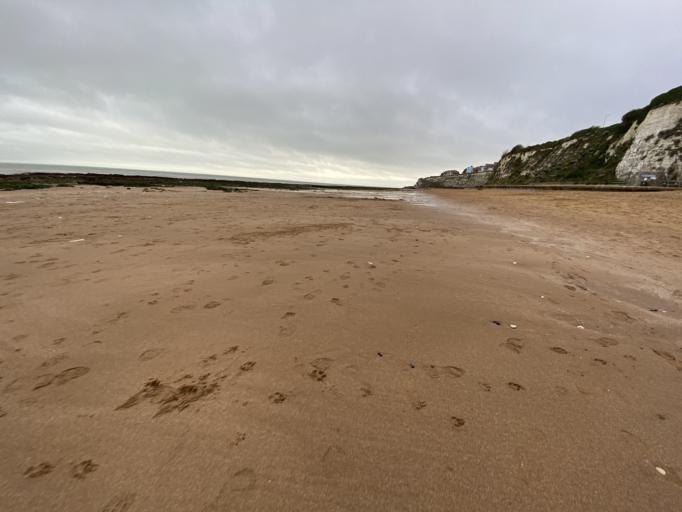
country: GB
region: England
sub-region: Kent
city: Broadstairs
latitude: 51.3657
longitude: 1.4457
